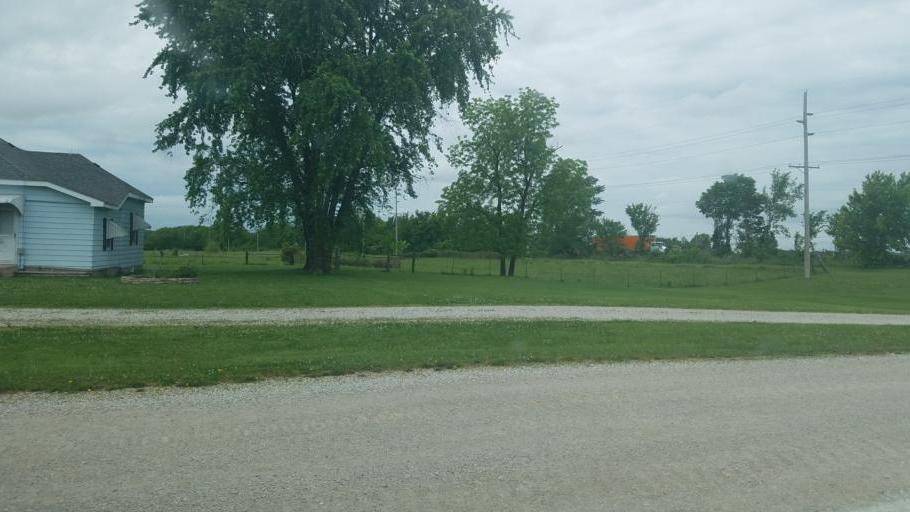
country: US
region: Missouri
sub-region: Morgan County
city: Versailles
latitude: 38.4469
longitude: -92.8045
